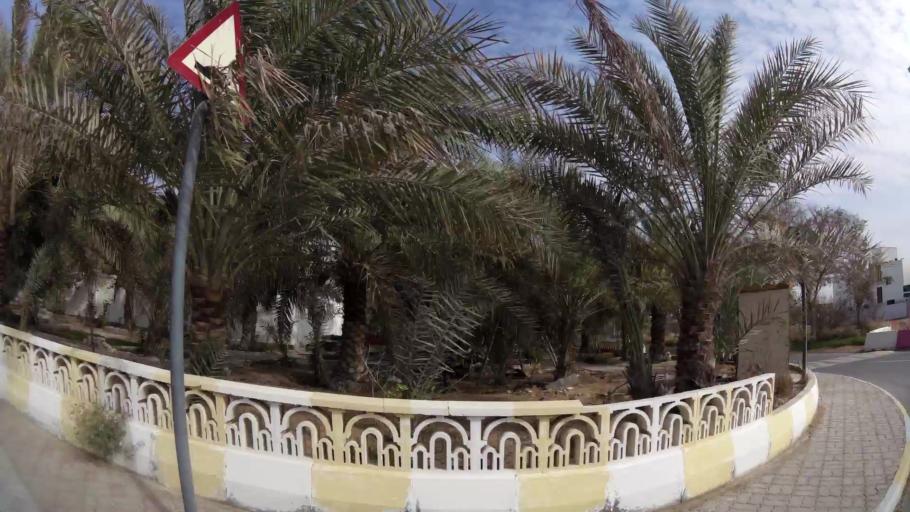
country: AE
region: Abu Dhabi
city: Abu Dhabi
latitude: 24.6081
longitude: 54.7002
